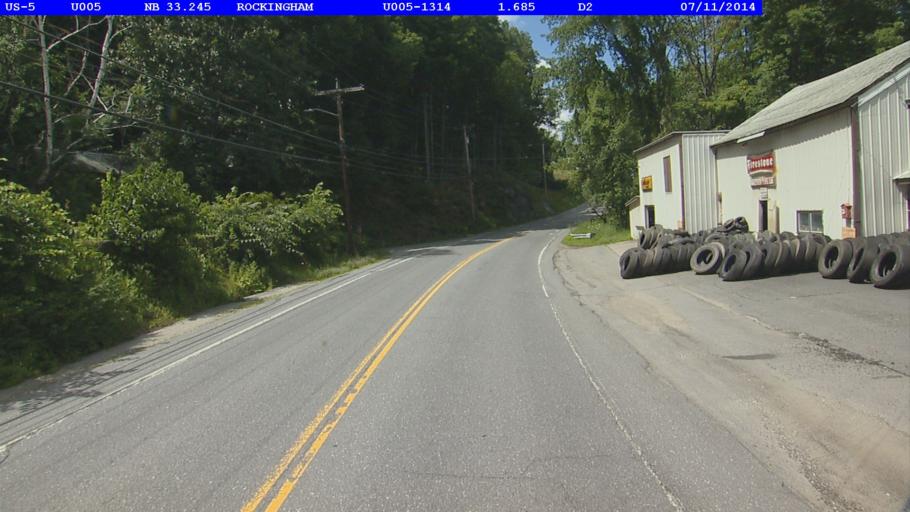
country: US
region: Vermont
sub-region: Windham County
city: Bellows Falls
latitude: 43.1456
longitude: -72.4582
